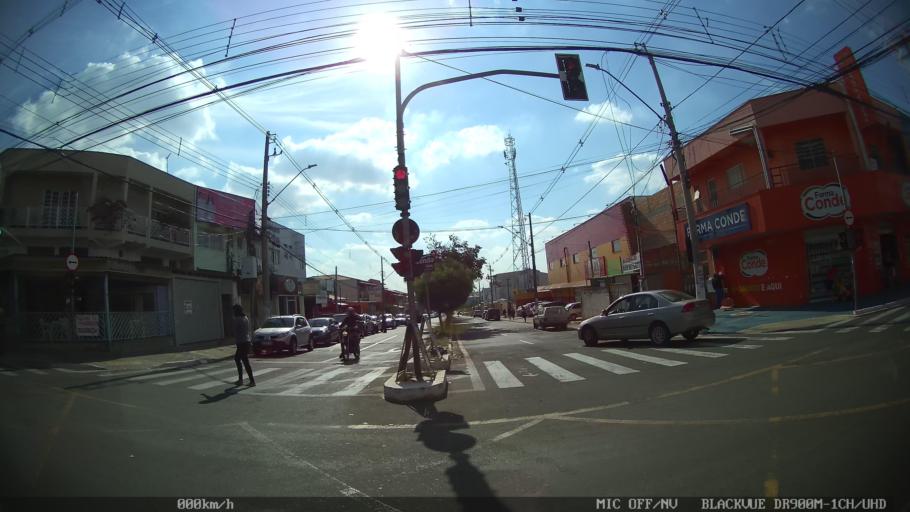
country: BR
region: Sao Paulo
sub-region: Hortolandia
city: Hortolandia
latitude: -22.9023
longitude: -47.2417
